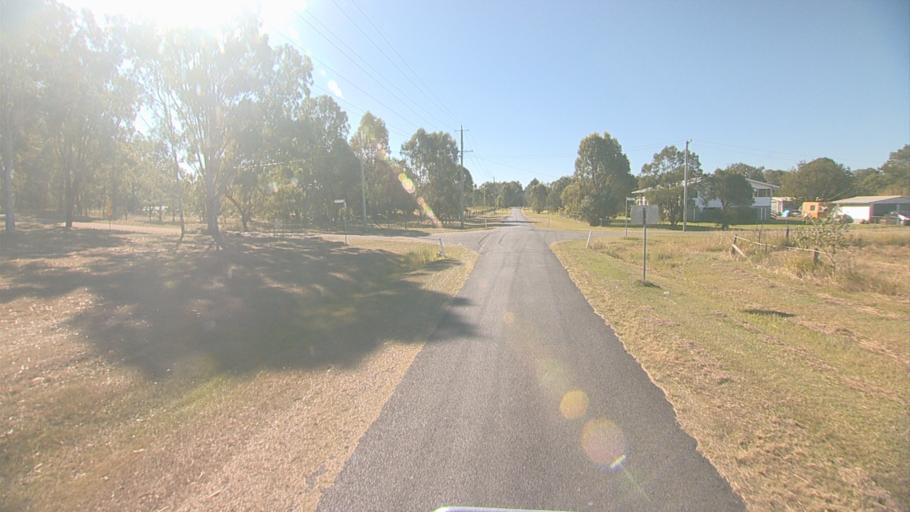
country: AU
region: Queensland
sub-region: Logan
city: North Maclean
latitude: -27.7803
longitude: 153.0191
